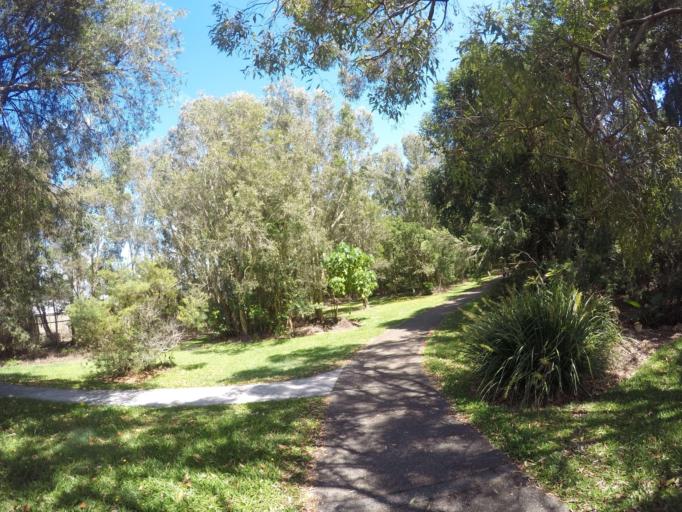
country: AU
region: Queensland
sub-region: Sunshine Coast
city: Mooloolaba
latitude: -26.6142
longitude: 153.0933
